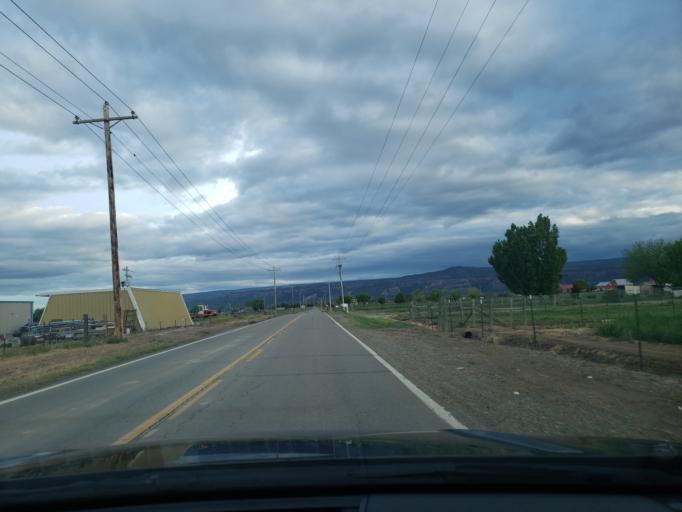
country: US
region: Colorado
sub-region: Mesa County
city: Fruita
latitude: 39.1908
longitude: -108.7013
